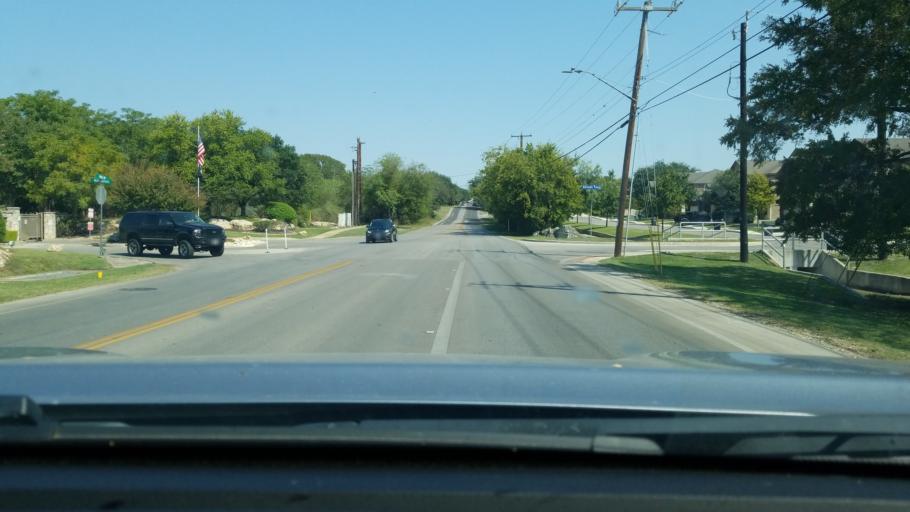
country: US
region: Texas
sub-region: Bexar County
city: Leon Valley
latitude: 29.5447
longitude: -98.6052
